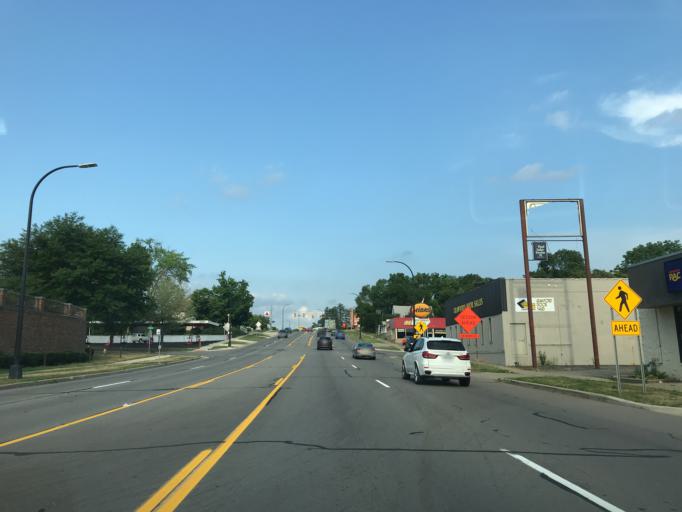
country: US
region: Michigan
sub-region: Washtenaw County
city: Ypsilanti
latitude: 42.2411
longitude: -83.6051
